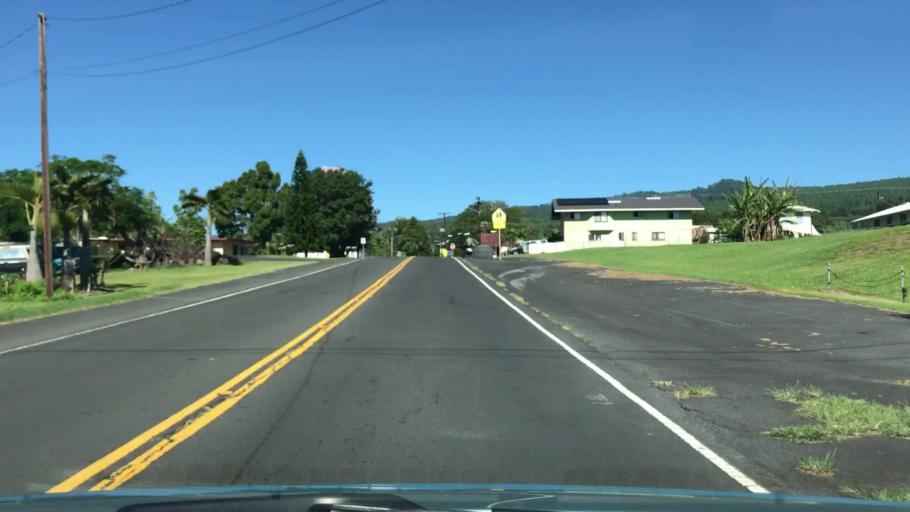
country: US
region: Hawaii
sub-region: Hawaii County
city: Pahala
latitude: 19.2025
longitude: -155.4758
